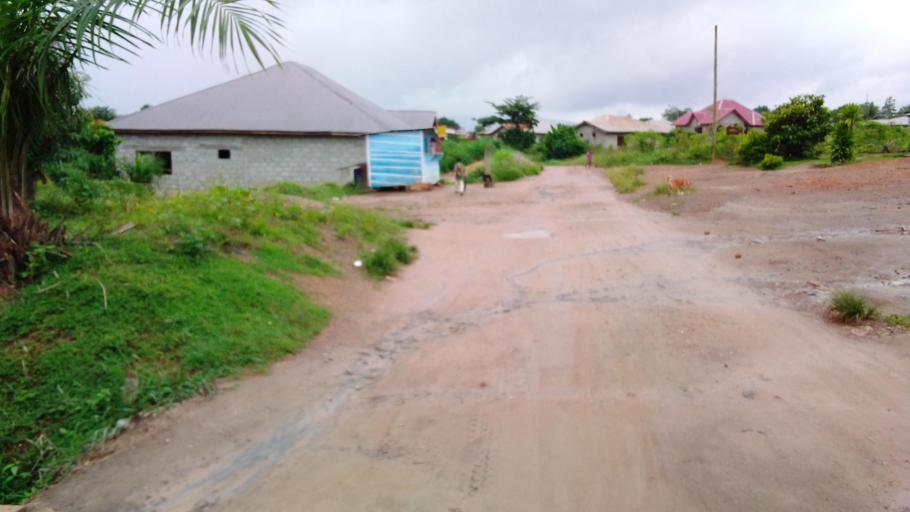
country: SL
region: Eastern Province
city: Kenema
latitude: 7.8603
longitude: -11.1705
